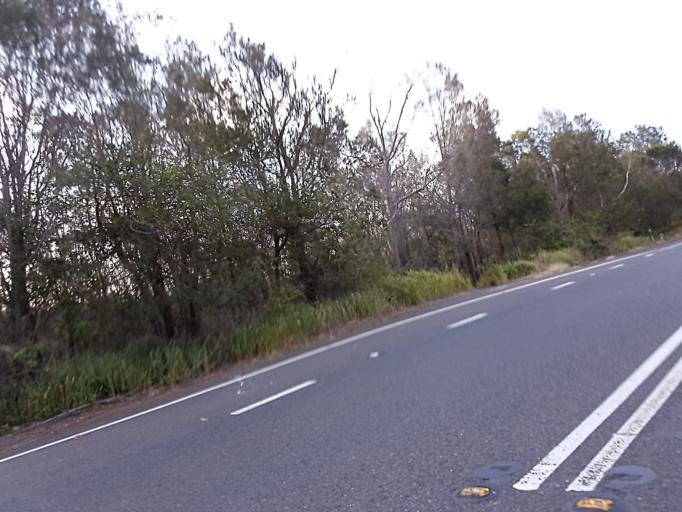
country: AU
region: New South Wales
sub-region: Warringah
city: Allambie Heights
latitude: -33.7788
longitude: 151.2391
